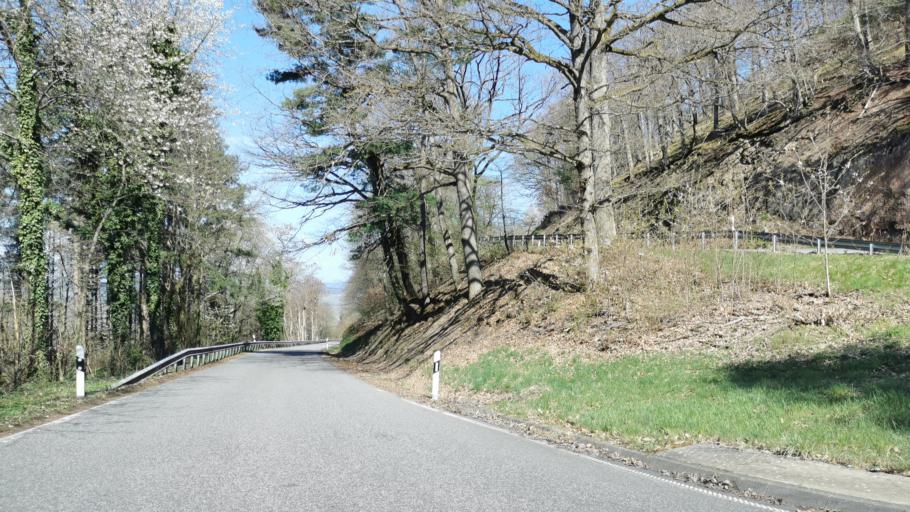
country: DE
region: Rheinland-Pfalz
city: Veldenz
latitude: 49.8824
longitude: 7.0227
